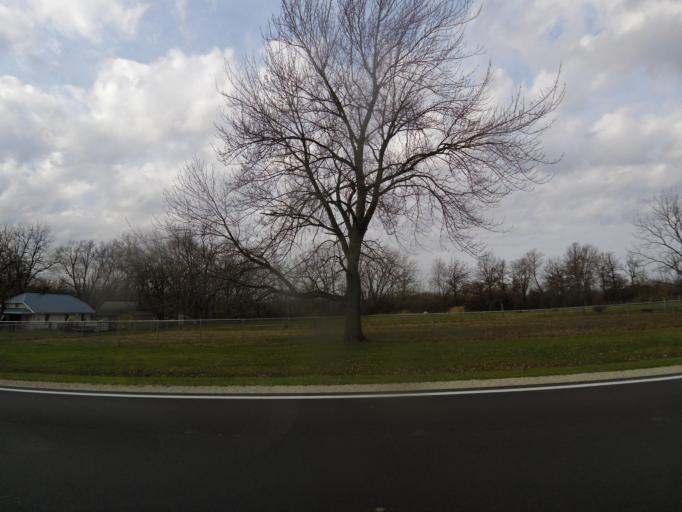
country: US
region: Illinois
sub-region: Christian County
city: Pana
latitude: 39.3716
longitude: -89.0817
